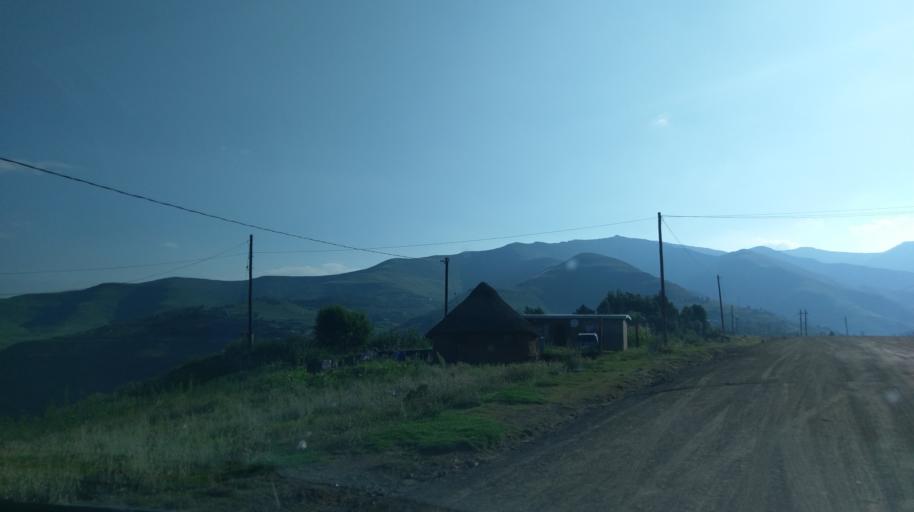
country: LS
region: Butha-Buthe
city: Butha-Buthe
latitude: -29.1060
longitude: 28.4974
